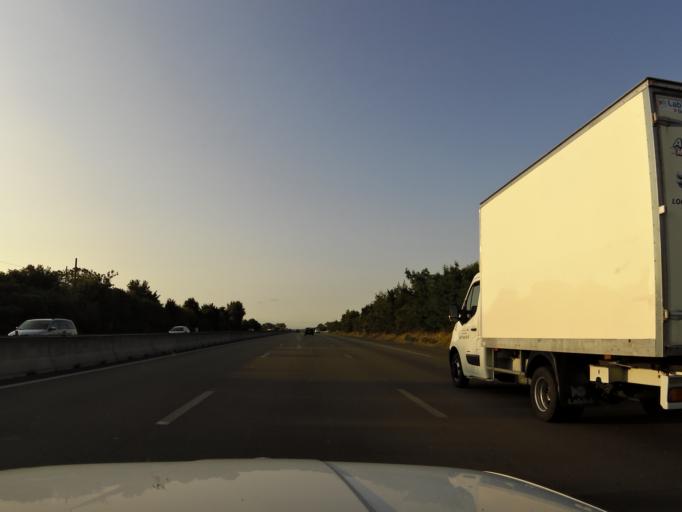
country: FR
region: Rhone-Alpes
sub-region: Departement de l'Isere
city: Auberives-sur-Vareze
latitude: 45.4393
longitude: 4.8256
